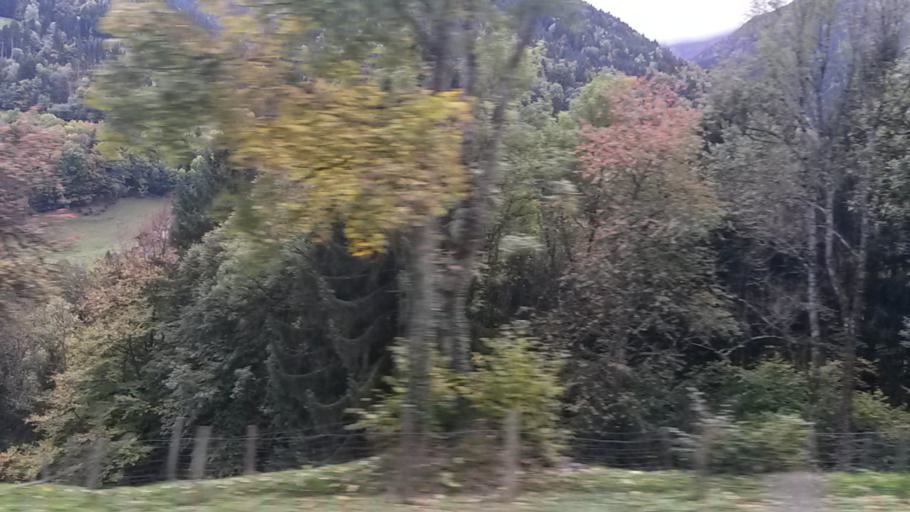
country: CH
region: Valais
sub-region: Monthey District
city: Troistorrents
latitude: 46.2191
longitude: 6.9039
